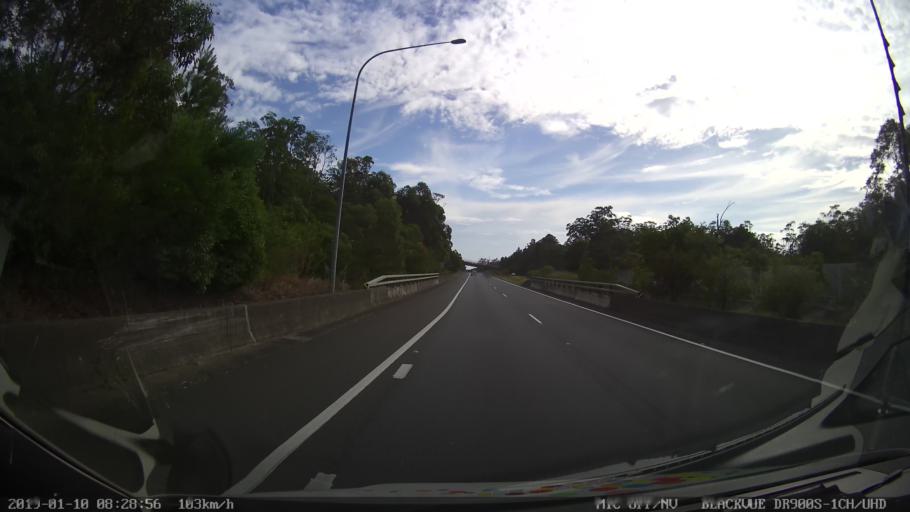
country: AU
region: New South Wales
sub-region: Coffs Harbour
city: Bonville
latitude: -30.3879
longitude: 153.0388
